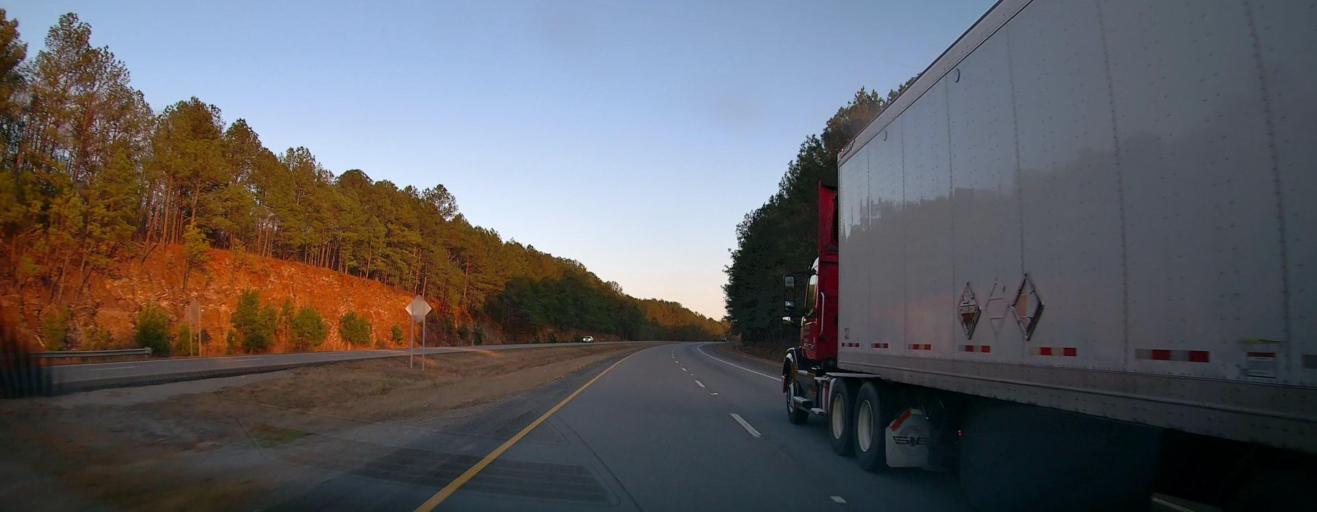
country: US
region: Alabama
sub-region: Coosa County
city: Goodwater
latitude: 33.0353
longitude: -86.1209
